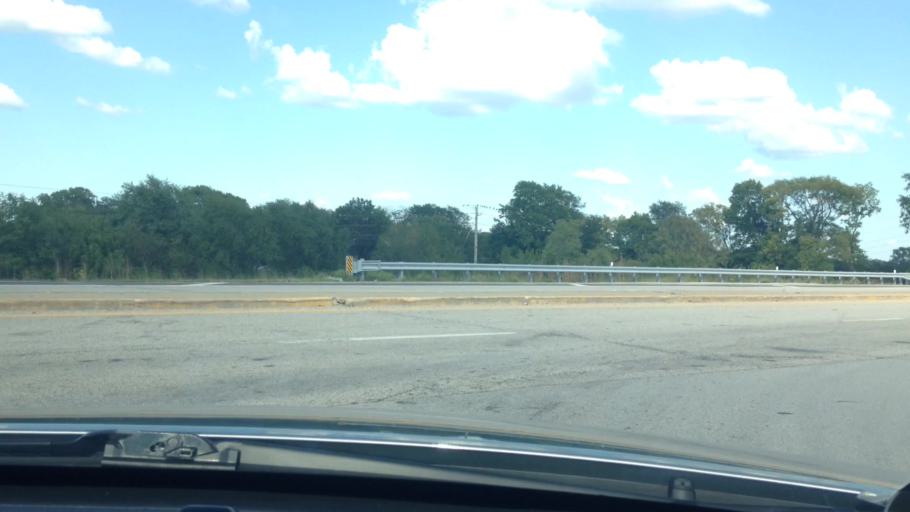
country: US
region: Missouri
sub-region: Clay County
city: Pleasant Valley
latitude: 39.3032
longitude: -94.5115
